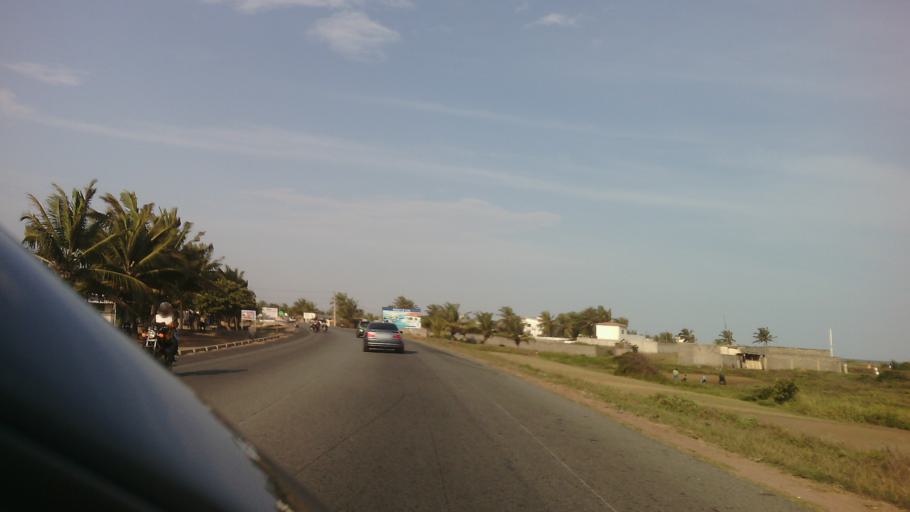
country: TG
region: Maritime
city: Lome
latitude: 6.1806
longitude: 1.3895
